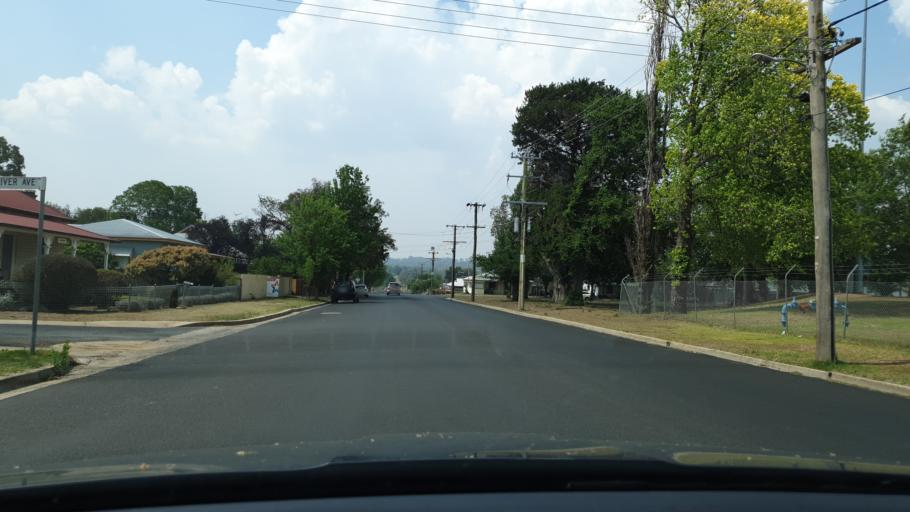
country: AU
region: New South Wales
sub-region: Armidale Dumaresq
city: Armidale
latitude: -30.5148
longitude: 151.6740
